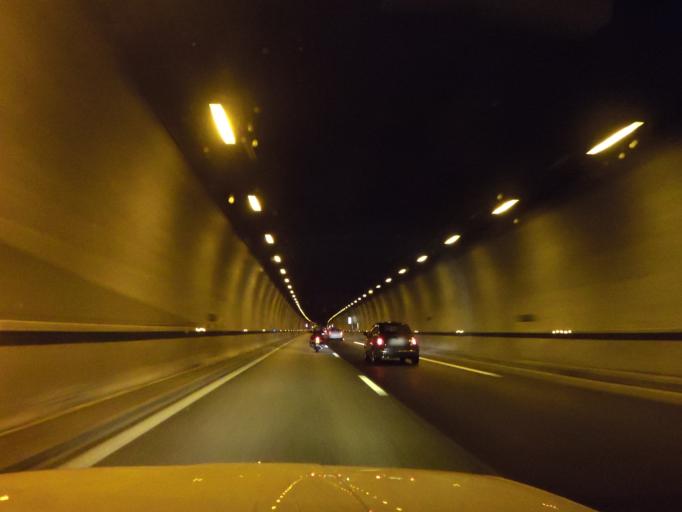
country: FR
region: Rhone-Alpes
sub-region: Departement de la Savoie
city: Novalaise
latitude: 45.5799
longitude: 5.8090
